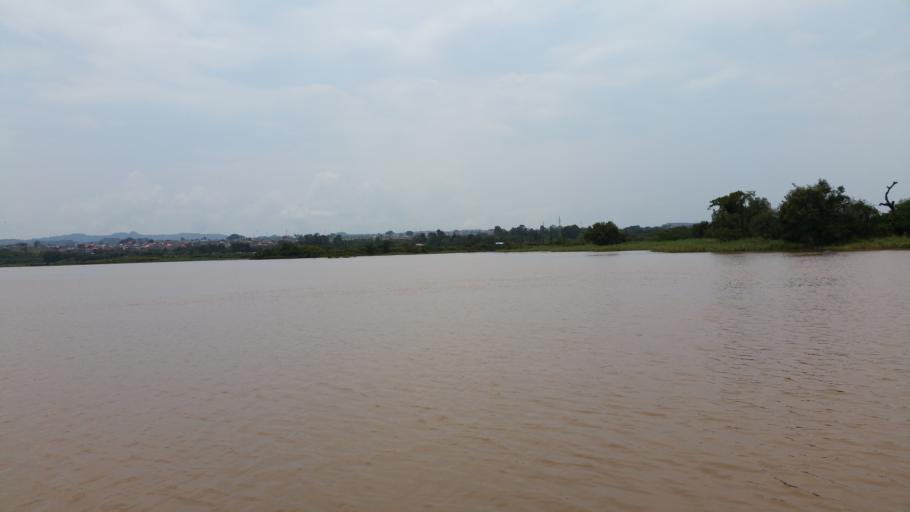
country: ET
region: Amhara
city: Bahir Dar
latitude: 11.6198
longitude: 37.4057
